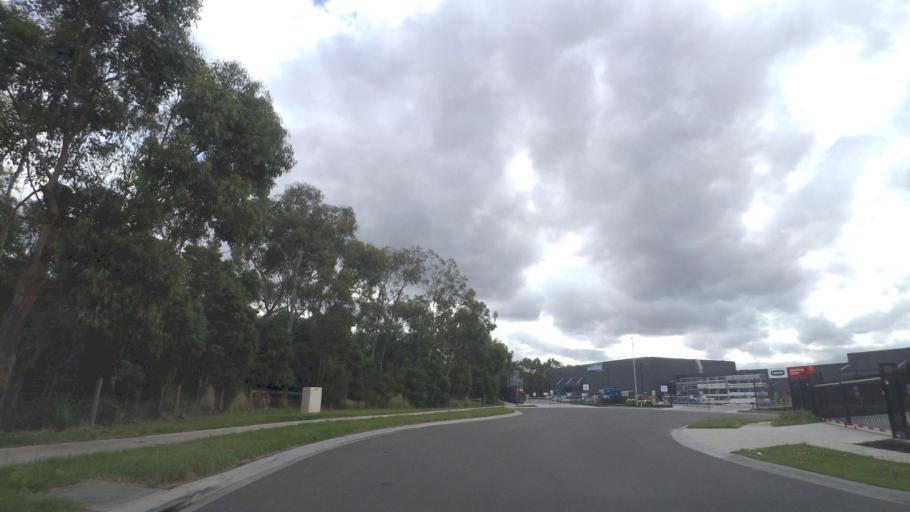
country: AU
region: Victoria
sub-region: Maroondah
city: Bayswater North
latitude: -37.8315
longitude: 145.2822
